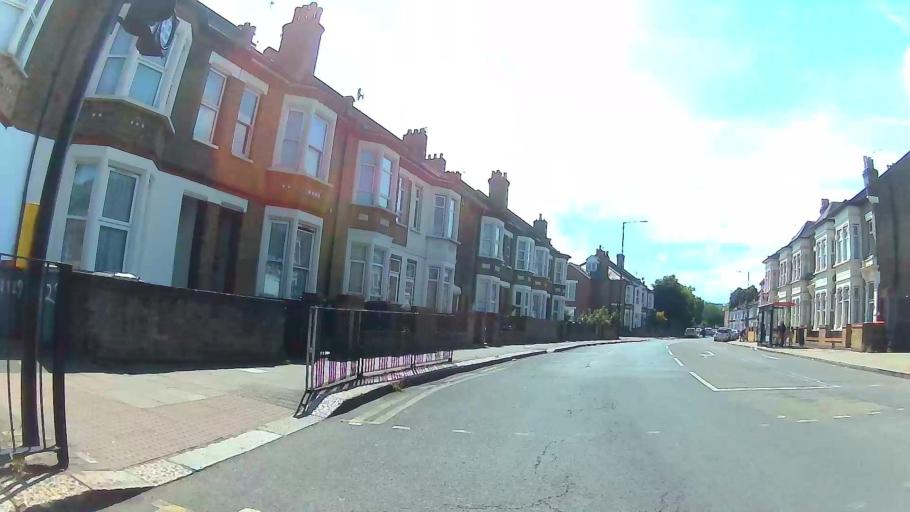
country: GB
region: England
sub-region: Greater London
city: East Ham
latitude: 51.5418
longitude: 0.0261
